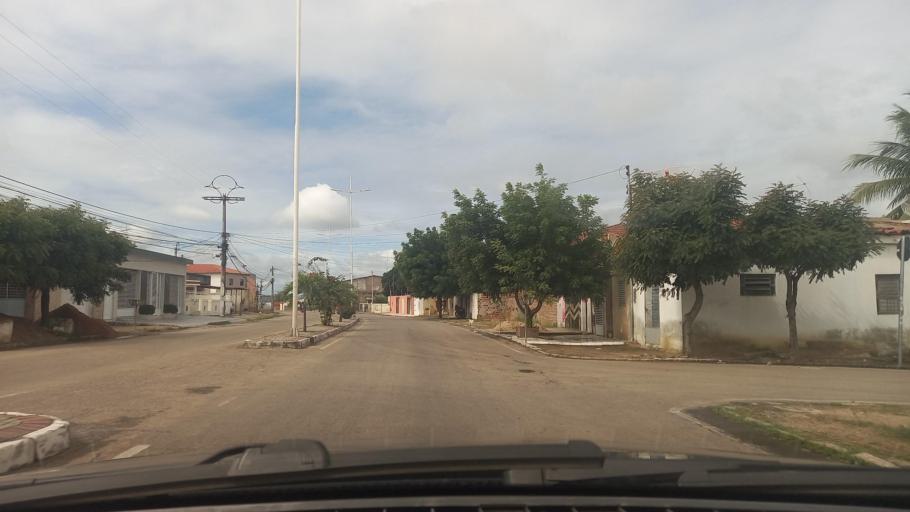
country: BR
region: Bahia
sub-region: Paulo Afonso
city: Paulo Afonso
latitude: -9.4380
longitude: -38.2069
